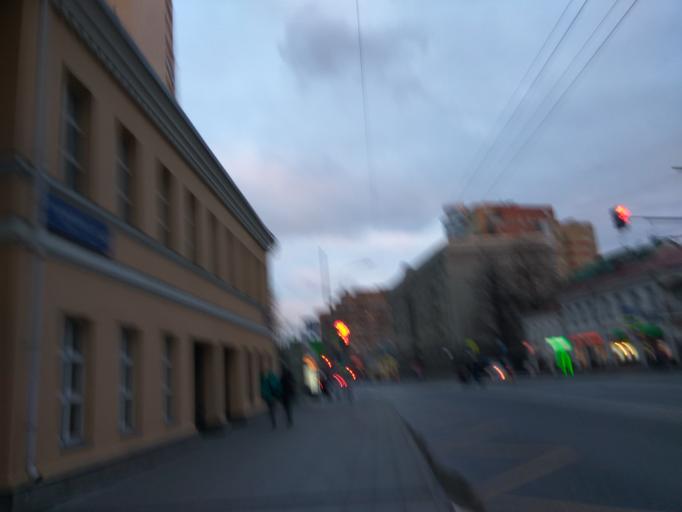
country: RU
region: Moscow
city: Taganskiy
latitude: 55.7398
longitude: 37.6642
